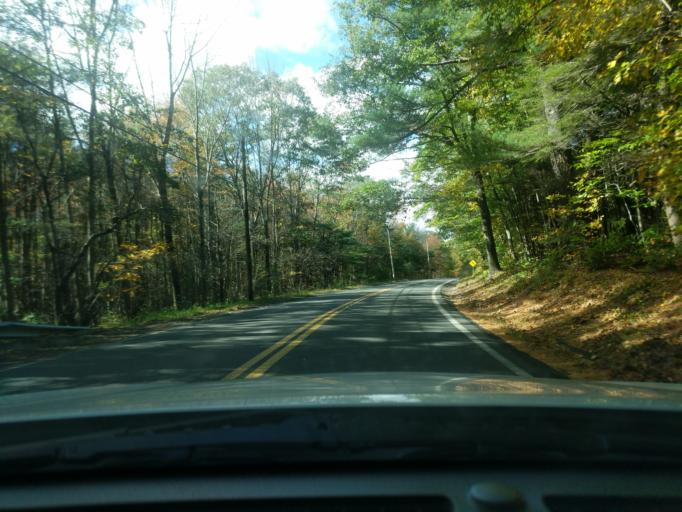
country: US
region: Massachusetts
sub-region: Berkshire County
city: Otis
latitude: 42.1704
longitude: -73.0151
